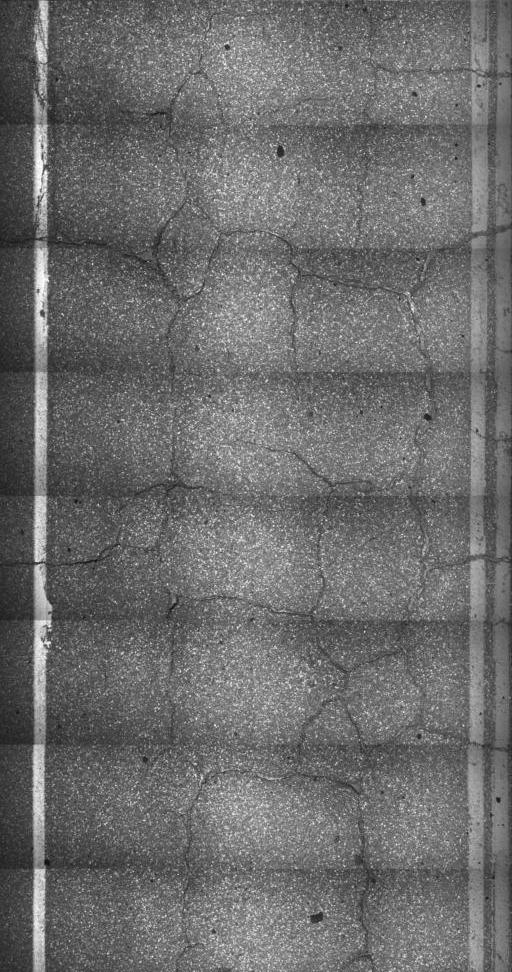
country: US
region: Vermont
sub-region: Windsor County
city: Windsor
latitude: 43.4882
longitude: -72.3857
